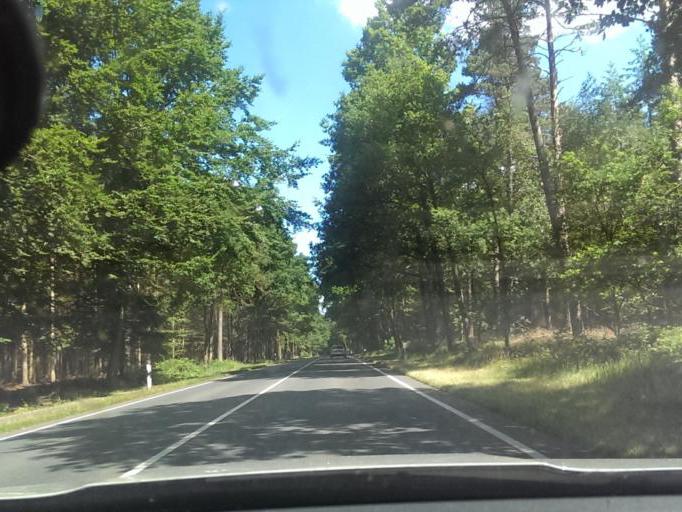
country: DE
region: Lower Saxony
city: Kirchlinteln
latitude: 52.9970
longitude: 9.2680
